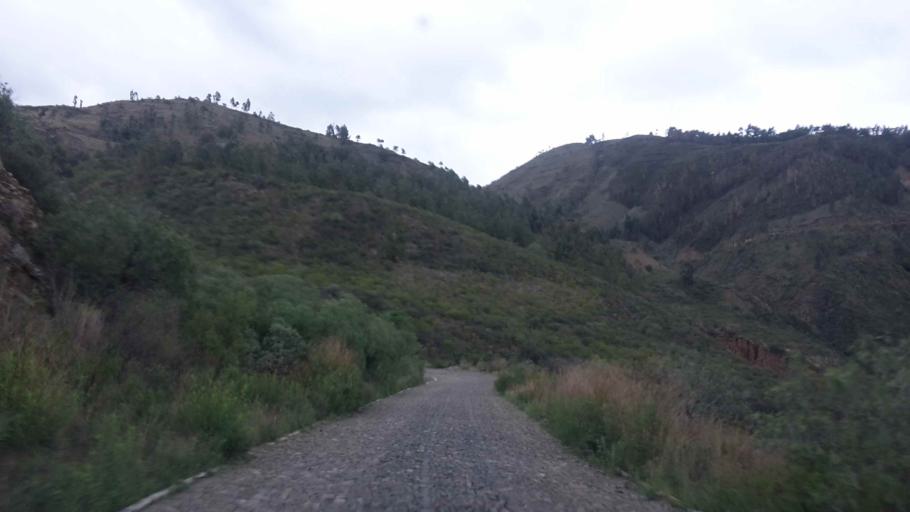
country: BO
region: Cochabamba
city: Cochabamba
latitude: -17.3673
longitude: -66.0625
